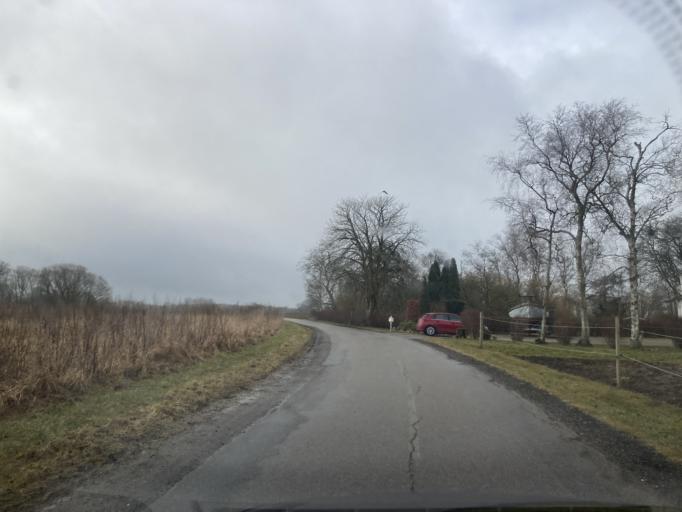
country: DK
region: Zealand
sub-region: Naestved Kommune
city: Fensmark
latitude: 55.2528
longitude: 11.8325
